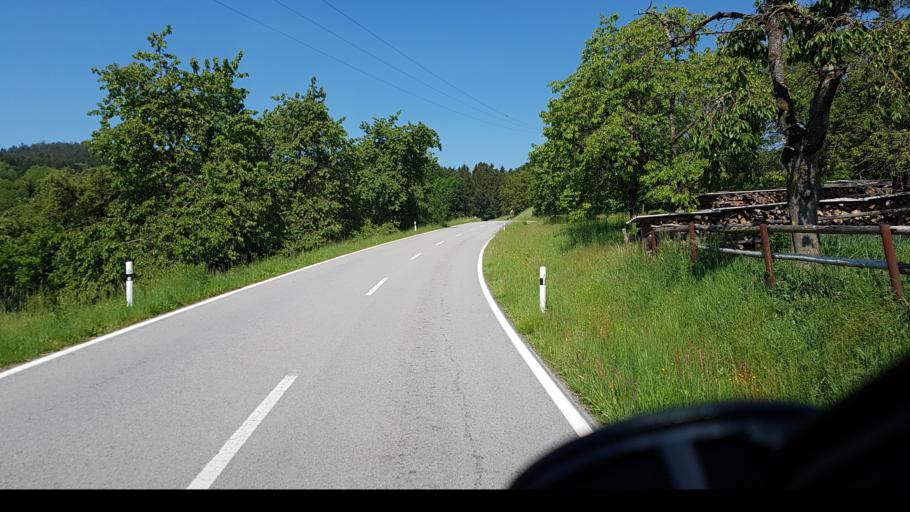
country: DE
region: Bavaria
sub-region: Lower Bavaria
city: Stubenberg
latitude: 48.2932
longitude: 13.0561
